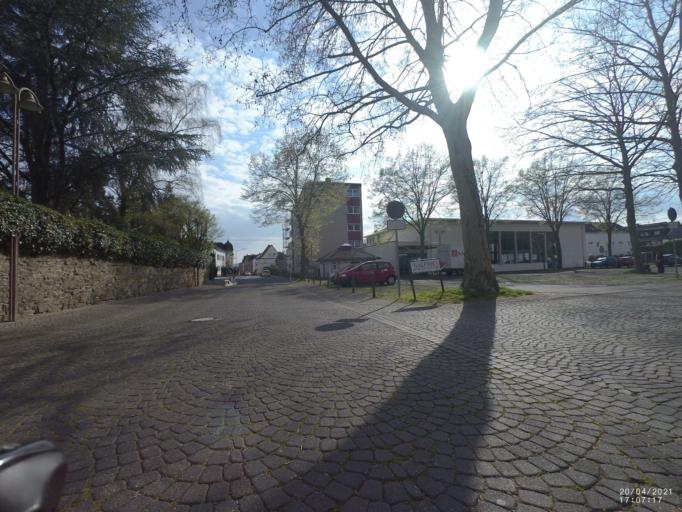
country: DE
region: Rheinland-Pfalz
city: Bendorf
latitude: 50.4200
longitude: 7.5763
